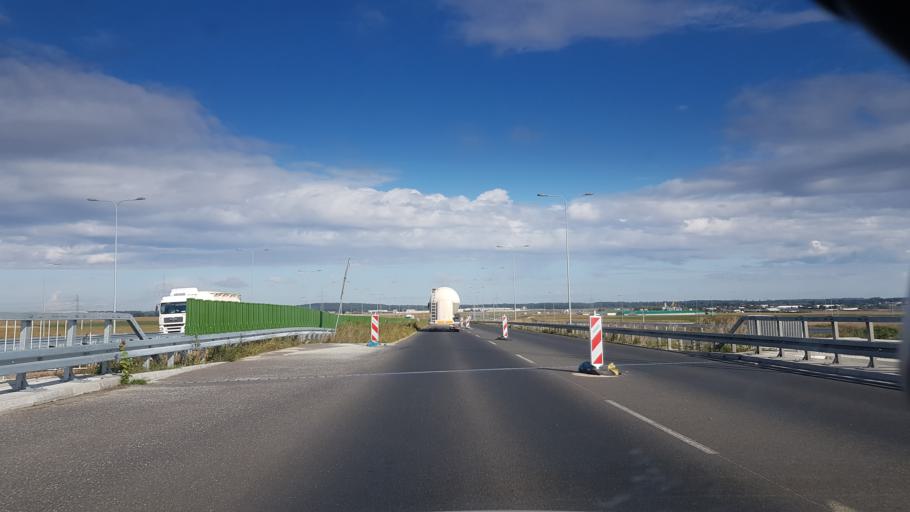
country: PL
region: Greater Poland Voivodeship
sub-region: Powiat poznanski
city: Steszew
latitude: 52.2674
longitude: 16.6682
